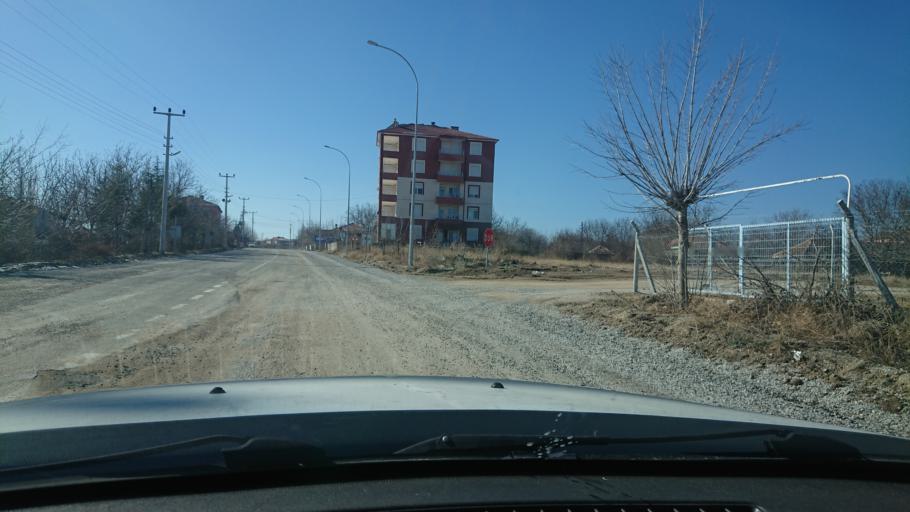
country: TR
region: Aksaray
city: Agacoren
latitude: 38.8705
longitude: 33.9087
